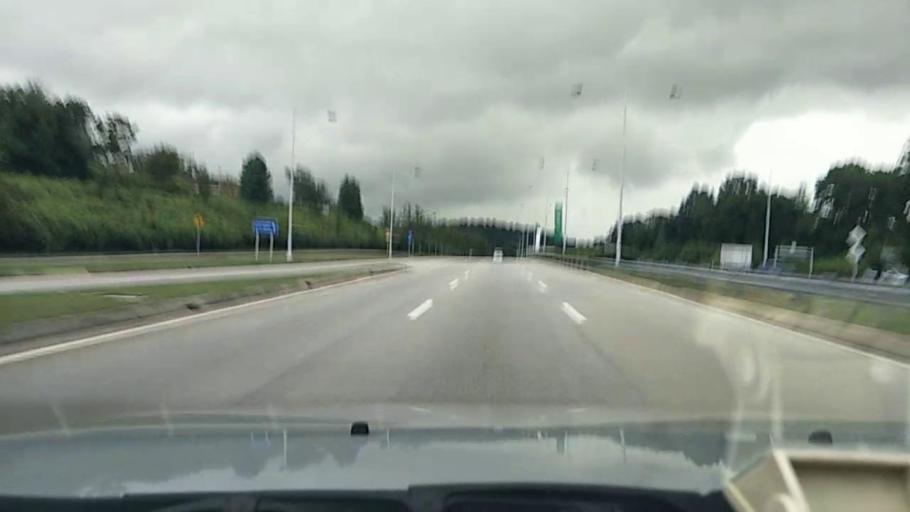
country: MY
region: Putrajaya
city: Putrajaya
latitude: 2.9445
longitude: 101.7138
